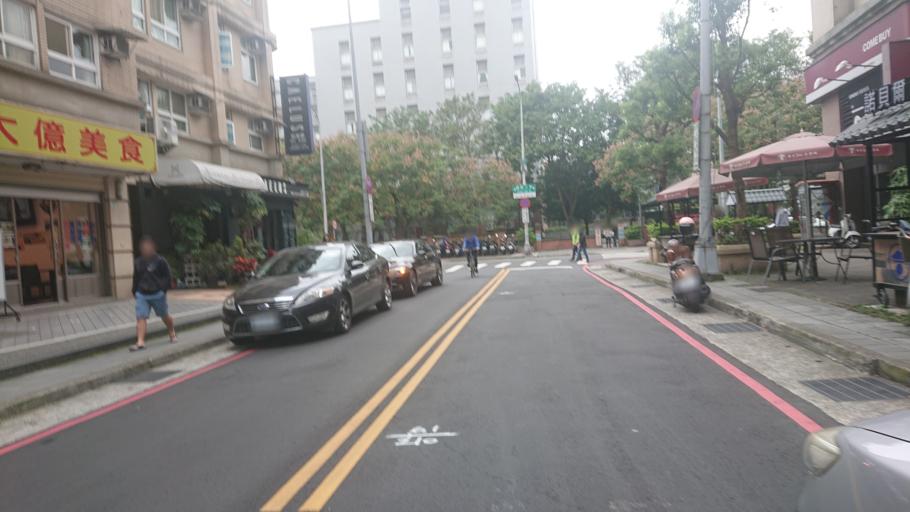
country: TW
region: Taiwan
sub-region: Taoyuan
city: Taoyuan
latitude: 24.9429
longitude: 121.3725
